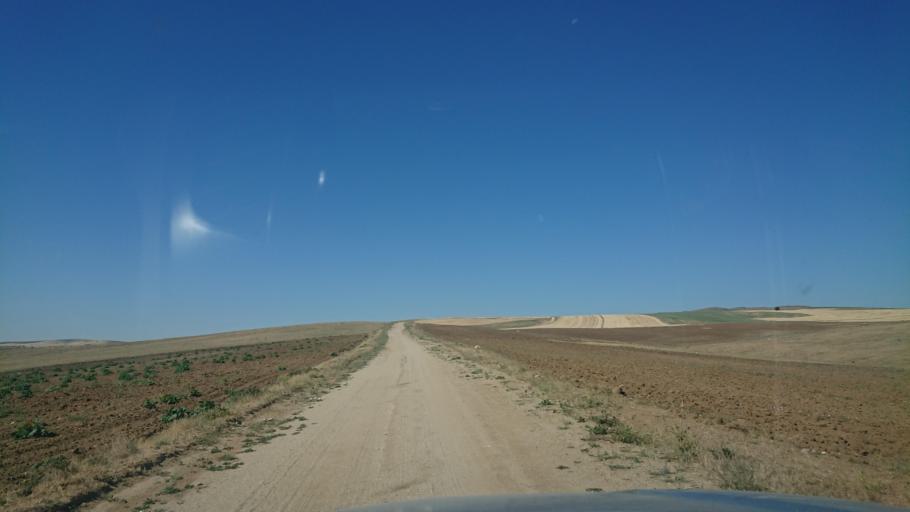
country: TR
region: Aksaray
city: Sariyahsi
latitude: 38.9296
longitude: 33.8560
